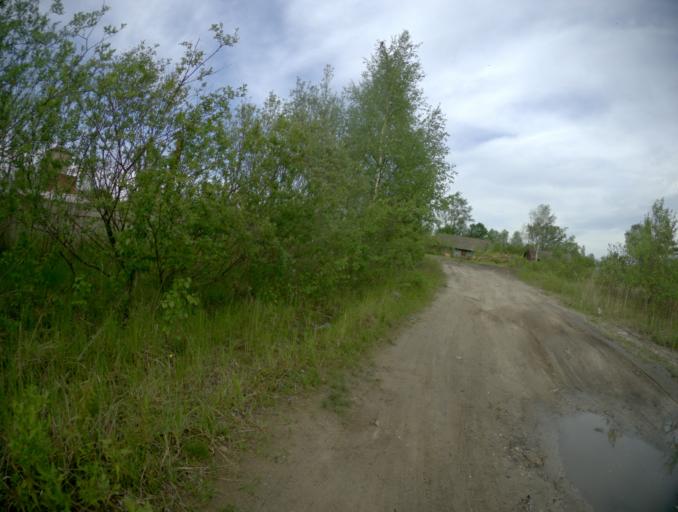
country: RU
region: Vladimir
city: Ivanishchi
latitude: 55.8402
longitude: 40.5201
